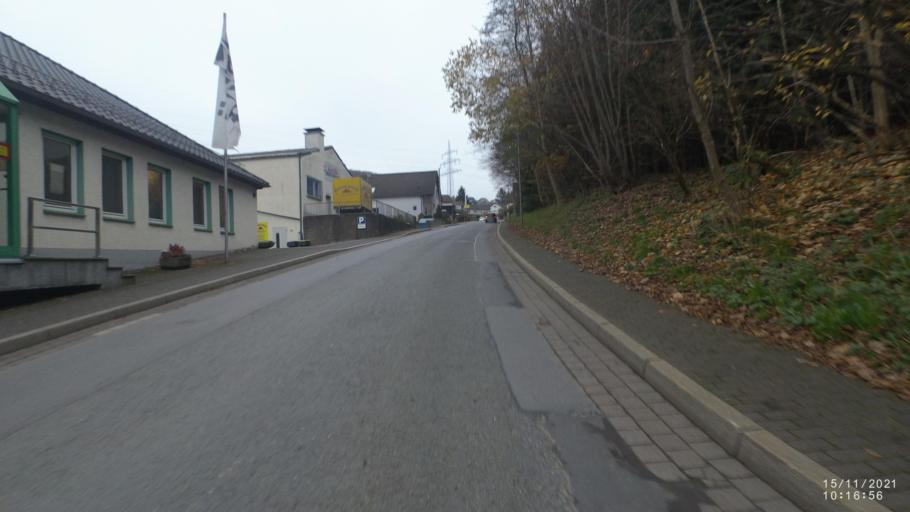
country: DE
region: North Rhine-Westphalia
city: Werdohl
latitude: 51.2403
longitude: 7.7703
